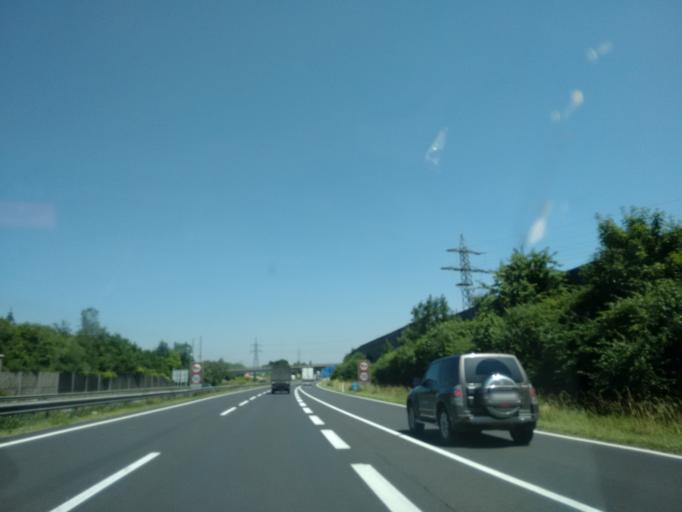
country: AT
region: Upper Austria
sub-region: Wels Stadt
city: Wels
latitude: 48.1812
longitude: 14.0020
